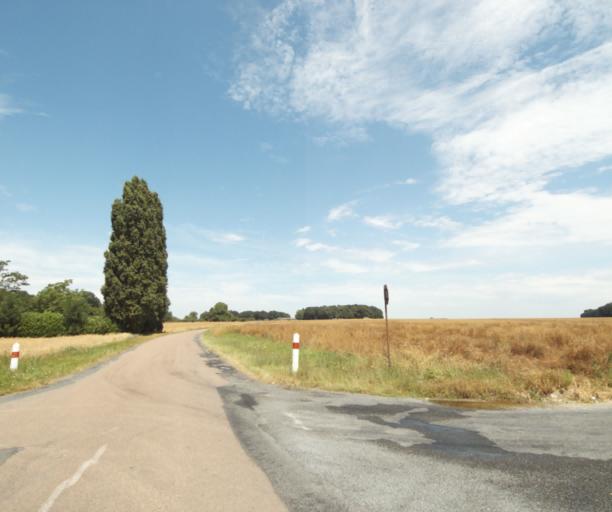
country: FR
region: Ile-de-France
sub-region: Departement de Seine-et-Marne
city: Cely
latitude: 48.4551
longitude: 2.5533
